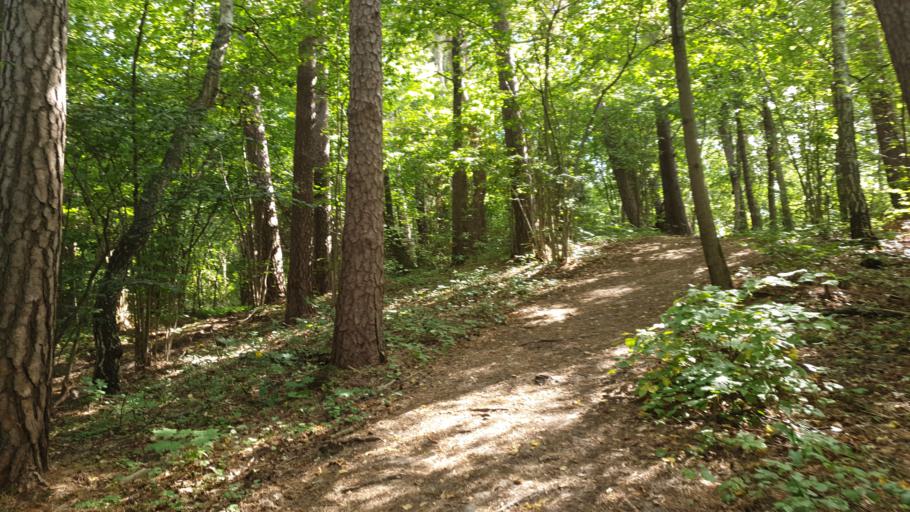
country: LT
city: Grigiskes
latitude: 54.8010
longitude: 24.9788
